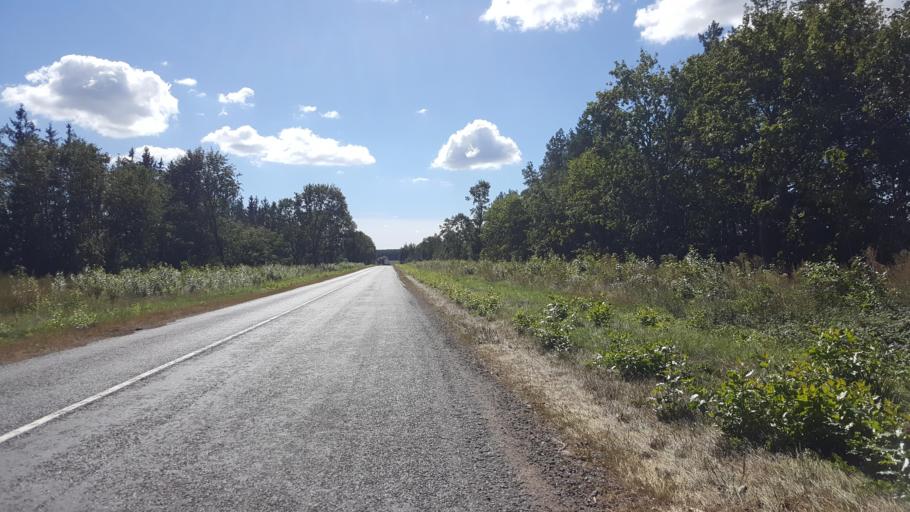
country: BY
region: Brest
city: Vysokaye
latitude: 52.3239
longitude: 23.3225
